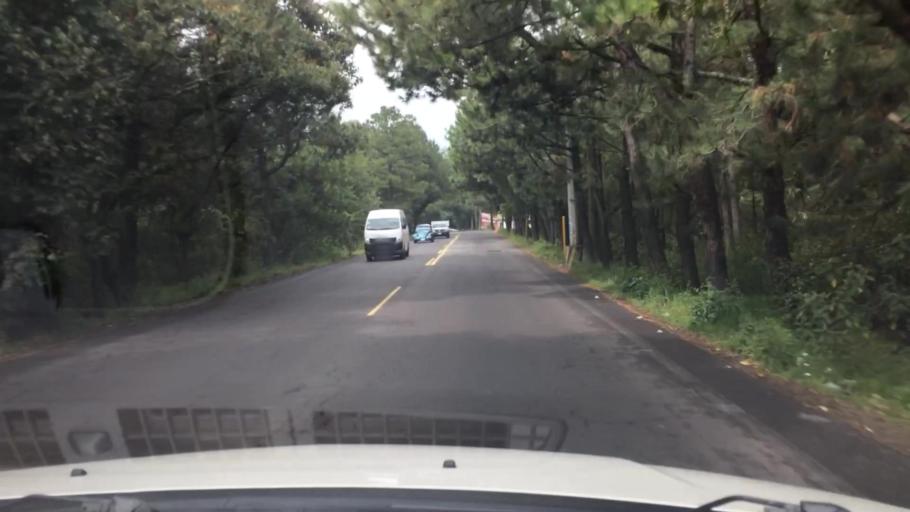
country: MX
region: Mexico City
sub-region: Tlalpan
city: Lomas de Tepemecatl
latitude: 19.2577
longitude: -99.2415
